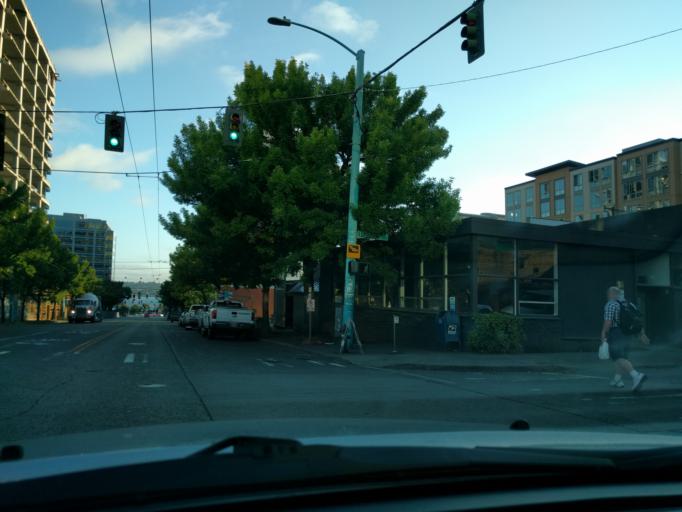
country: US
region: Washington
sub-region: King County
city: Seattle
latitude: 47.6207
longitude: -122.3342
